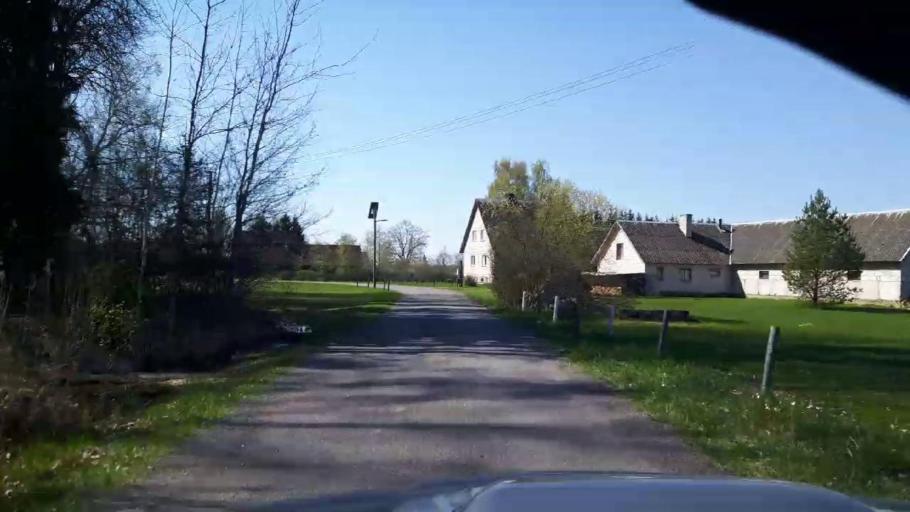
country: EE
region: Paernumaa
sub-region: Tootsi vald
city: Tootsi
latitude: 58.4707
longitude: 24.7870
